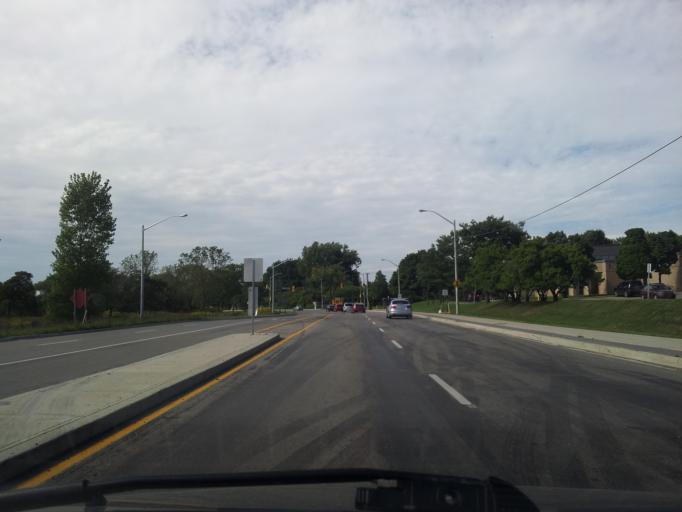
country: CA
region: Ontario
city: Kitchener
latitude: 43.4316
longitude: -80.4709
